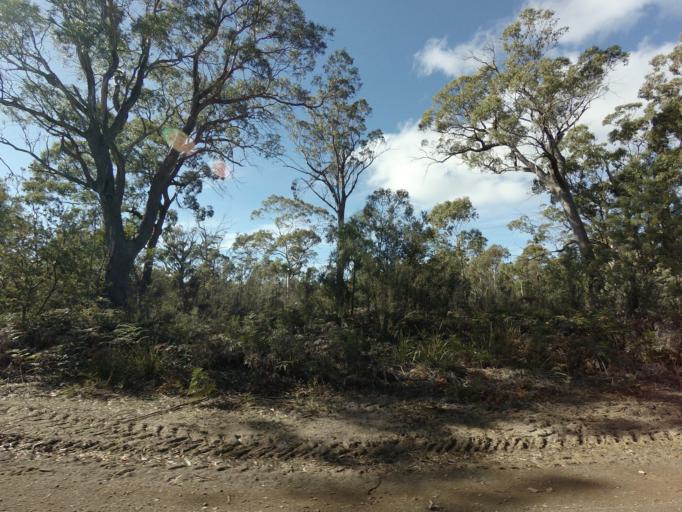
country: AU
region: Tasmania
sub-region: Clarence
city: Sandford
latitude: -42.9601
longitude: 147.7035
